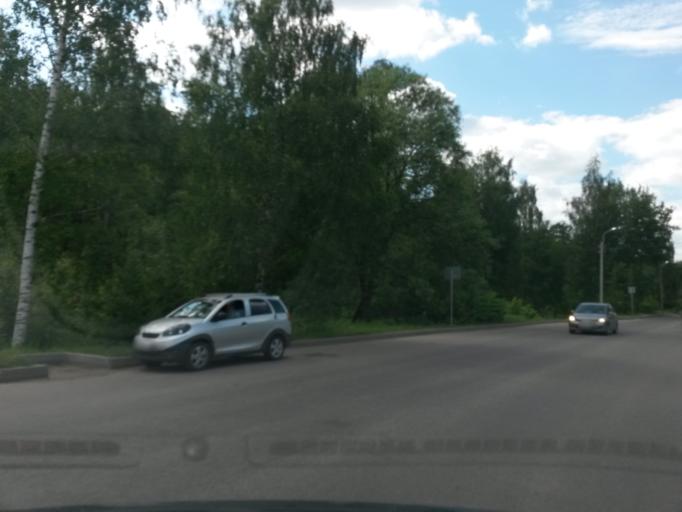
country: RU
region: Jaroslavl
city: Yaroslavl
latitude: 57.6431
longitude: 39.9434
